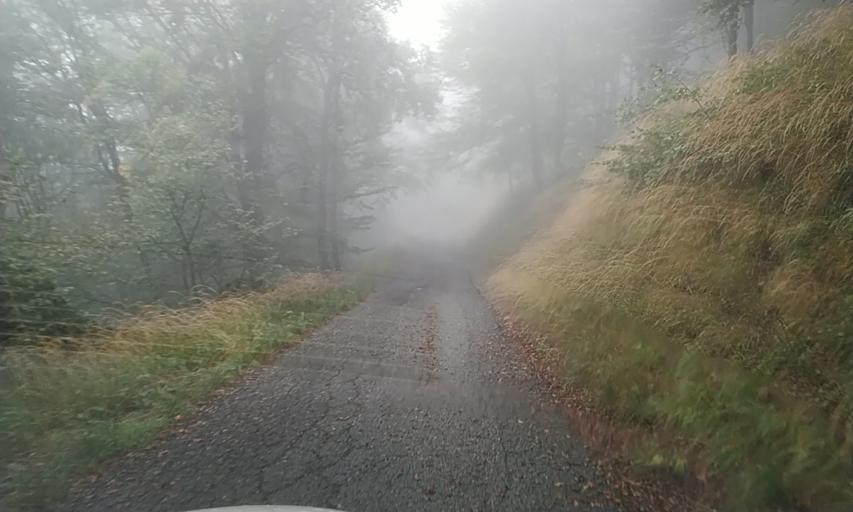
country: IT
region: Piedmont
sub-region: Provincia di Vercelli
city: Civiasco
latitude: 45.8351
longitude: 8.3180
